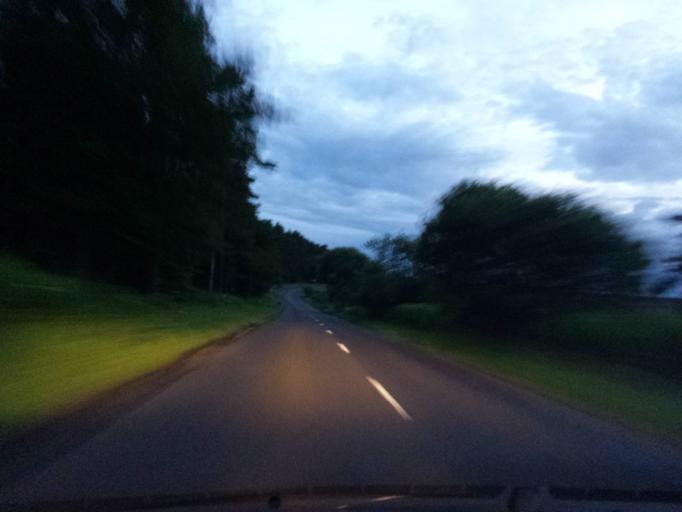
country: GB
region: Scotland
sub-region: The Scottish Borders
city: Duns
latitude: 55.7295
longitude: -2.4436
